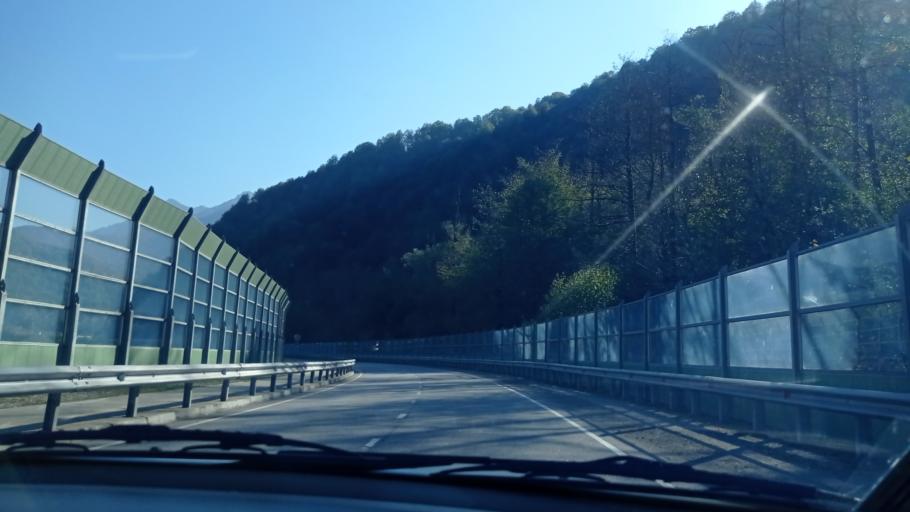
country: RU
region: Krasnodarskiy
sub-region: Sochi City
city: Krasnaya Polyana
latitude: 43.6945
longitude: 40.2692
